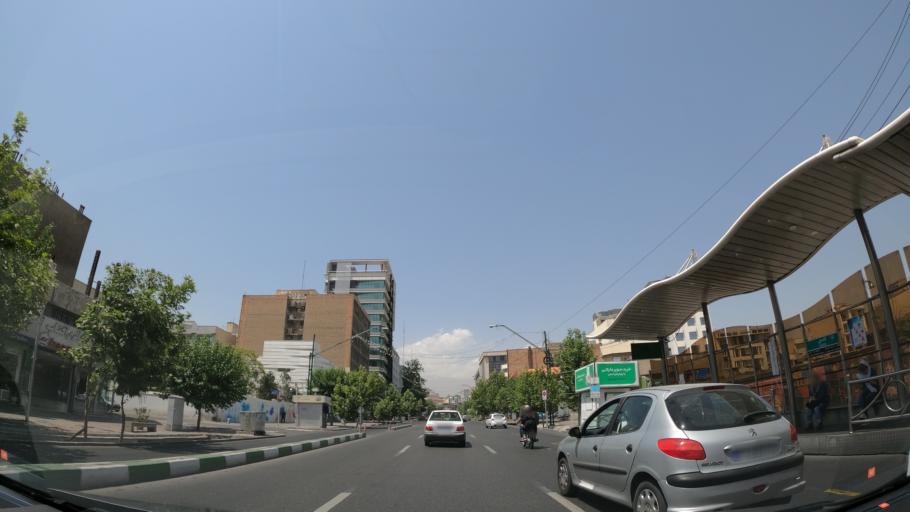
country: IR
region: Tehran
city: Tehran
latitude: 35.7246
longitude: 51.4140
